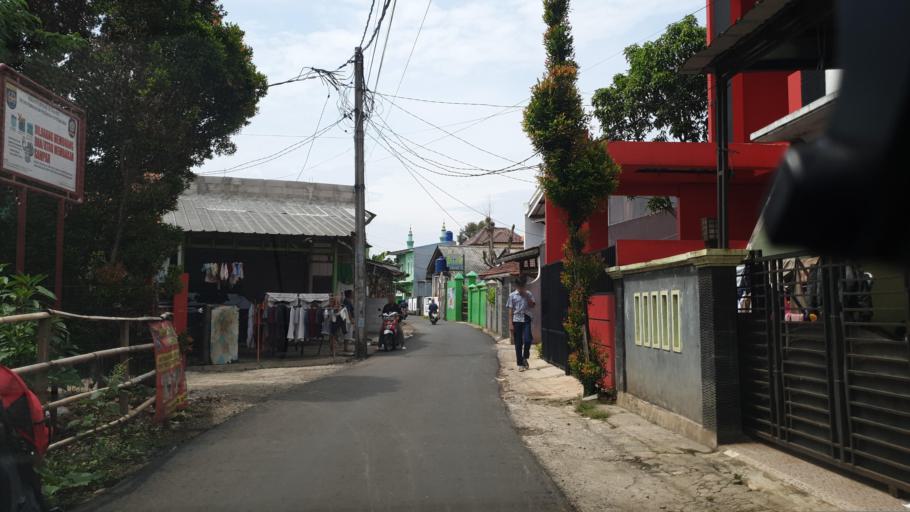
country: ID
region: West Java
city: Sawangan
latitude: -6.3721
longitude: 106.7616
